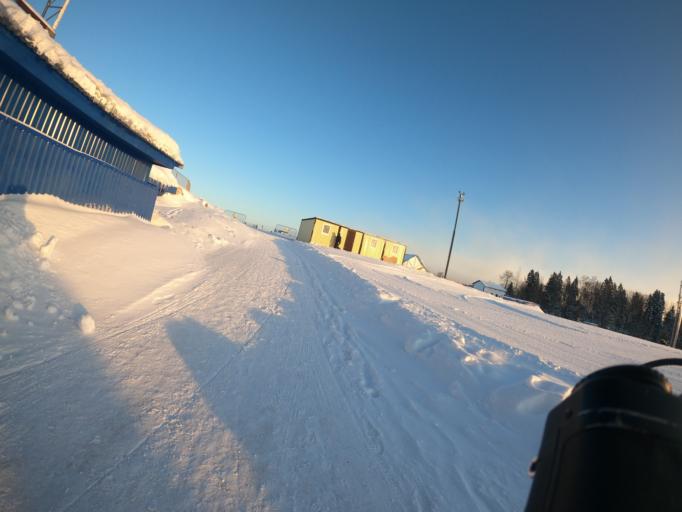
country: RU
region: Moskovskaya
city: Dedenevo
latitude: 56.2771
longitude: 37.5671
